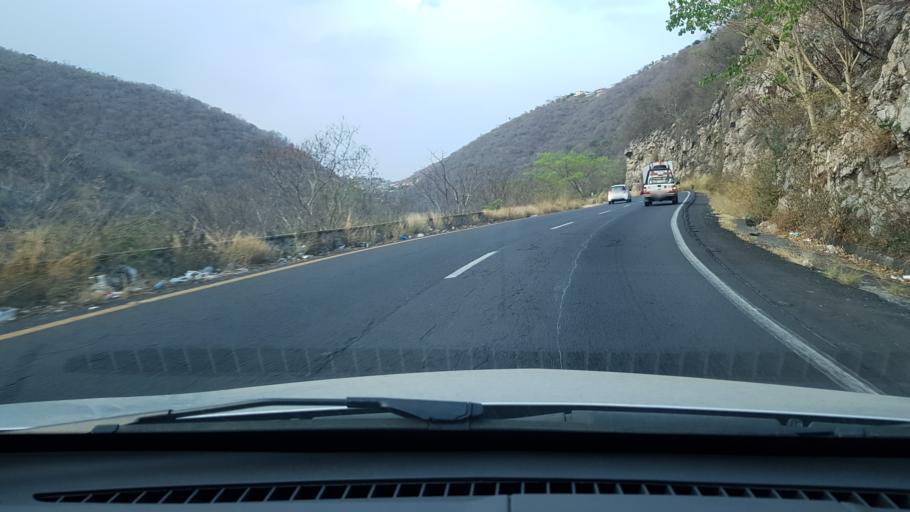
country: MX
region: Morelos
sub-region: Jiutepec
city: Independencia
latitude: 18.8645
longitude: -99.1213
